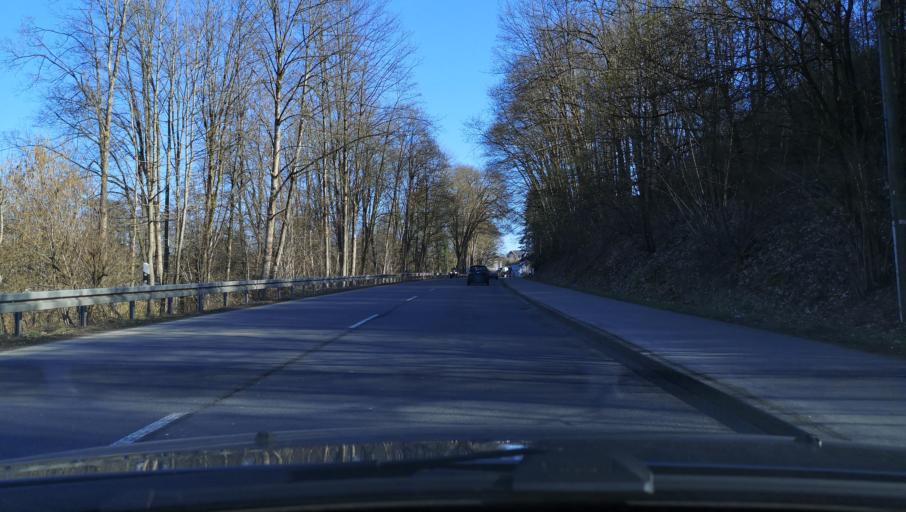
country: DE
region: North Rhine-Westphalia
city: Wipperfurth
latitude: 51.1226
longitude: 7.3711
